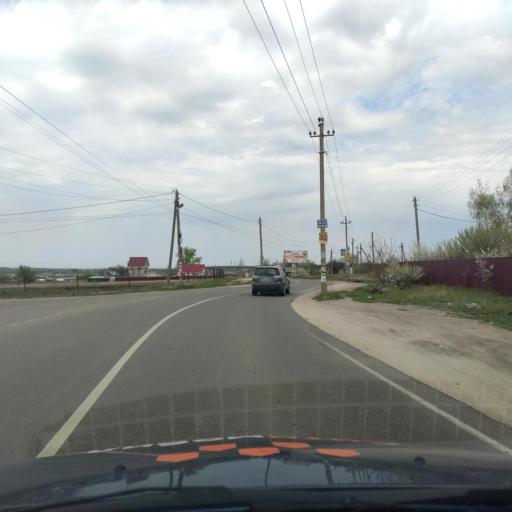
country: RU
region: Voronezj
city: Podgornoye
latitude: 51.8457
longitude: 39.1461
